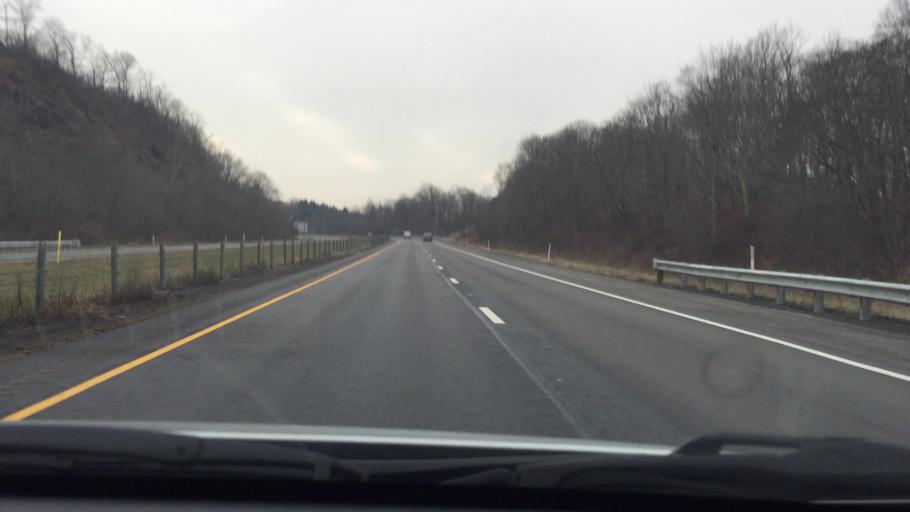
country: US
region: Pennsylvania
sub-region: Beaver County
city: Beaver
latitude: 40.6548
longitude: -80.3247
